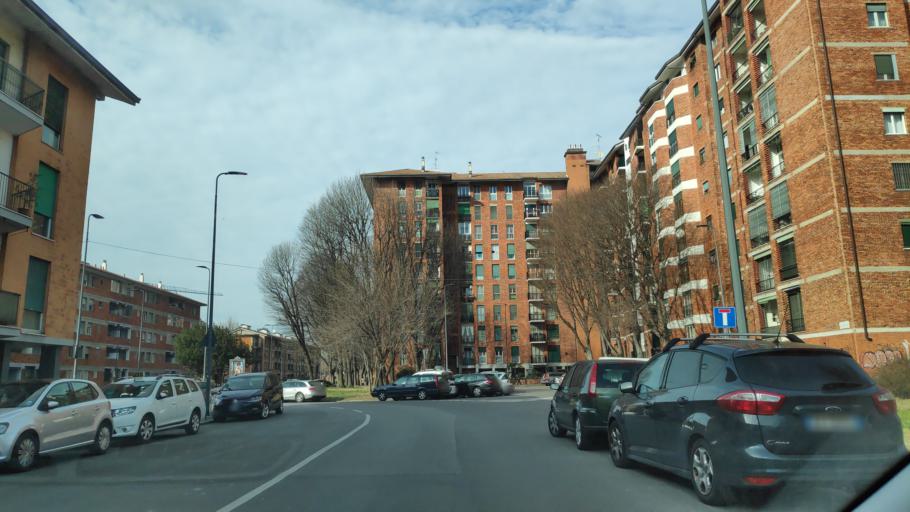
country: IT
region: Lombardy
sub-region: Citta metropolitana di Milano
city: Novegro-Tregarezzo-San Felice
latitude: 45.4890
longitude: 9.2440
